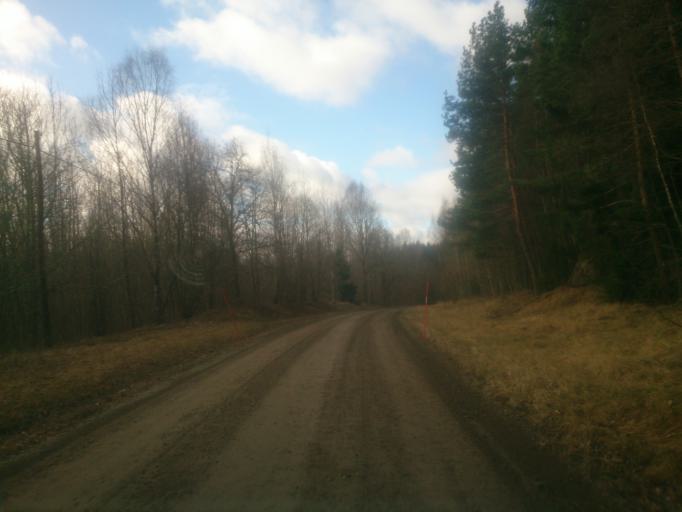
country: SE
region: OEstergoetland
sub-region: Atvidabergs Kommun
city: Atvidaberg
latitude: 58.1884
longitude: 16.1465
